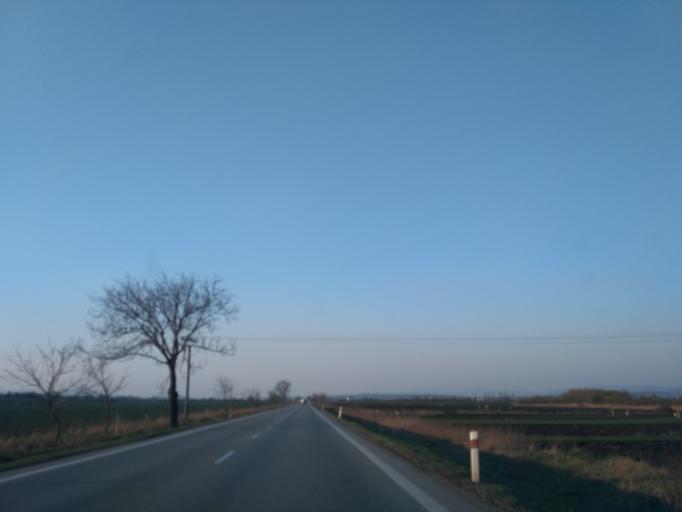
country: SK
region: Kosicky
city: Kosice
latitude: 48.6031
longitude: 21.2623
